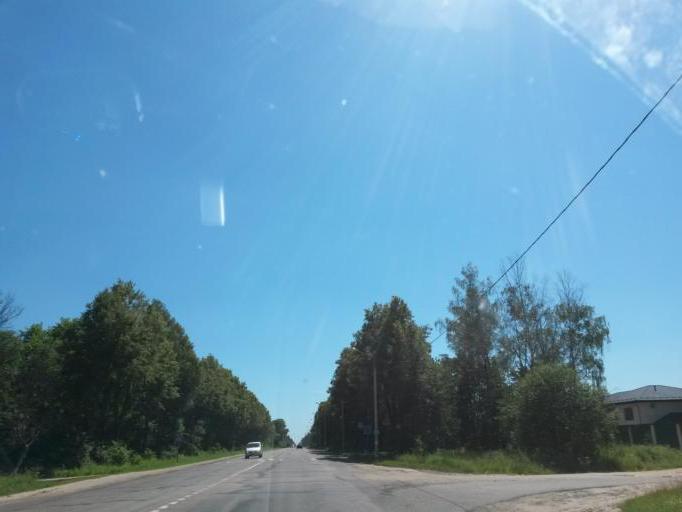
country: RU
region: Moskovskaya
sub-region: Chekhovskiy Rayon
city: Chekhov
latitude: 55.0810
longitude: 37.4399
